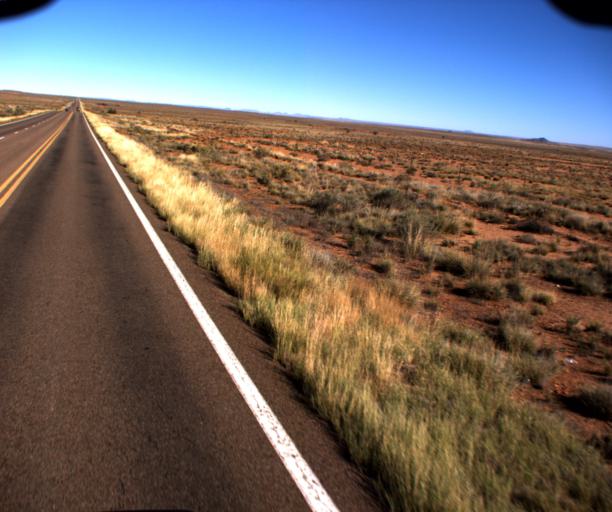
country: US
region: Arizona
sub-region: Navajo County
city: Snowflake
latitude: 34.7011
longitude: -110.1088
